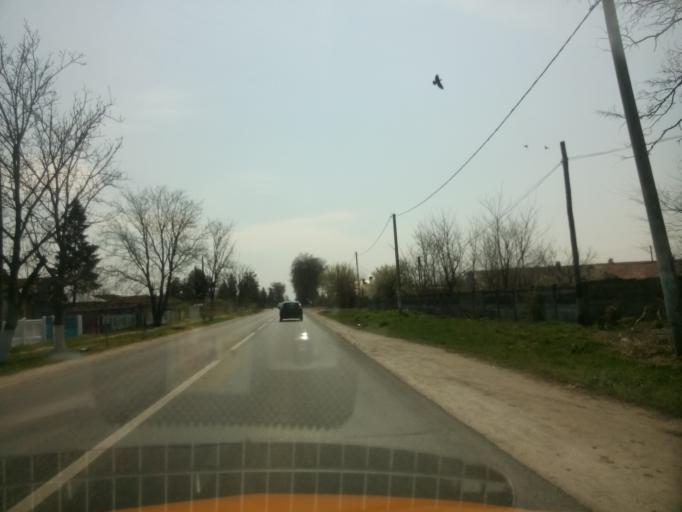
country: RO
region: Calarasi
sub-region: Comuna Frumusani
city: Frumusani
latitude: 44.2805
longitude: 26.3321
